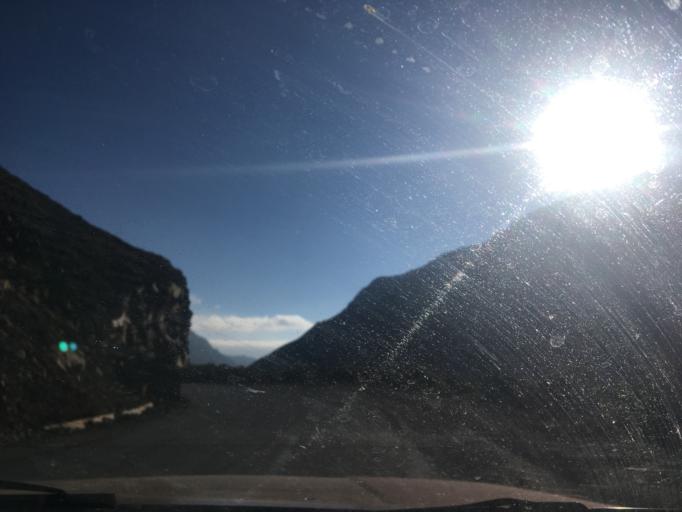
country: BO
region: La Paz
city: Quime
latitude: -17.0198
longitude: -67.2802
